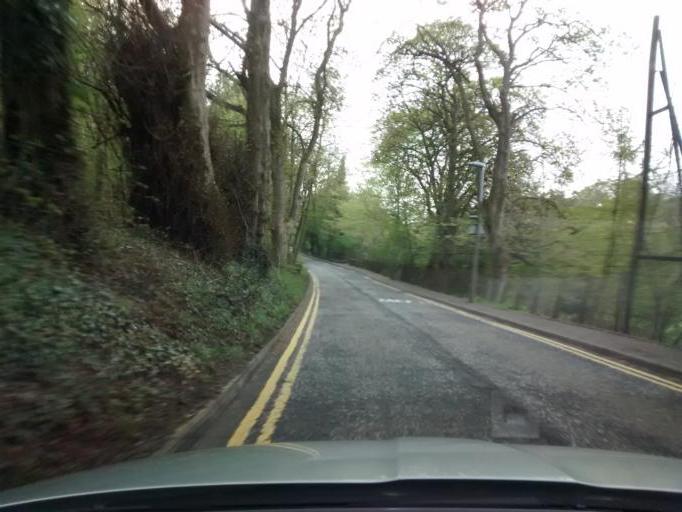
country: GB
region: Scotland
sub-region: Edinburgh
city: Colinton
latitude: 55.9188
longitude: -3.2309
